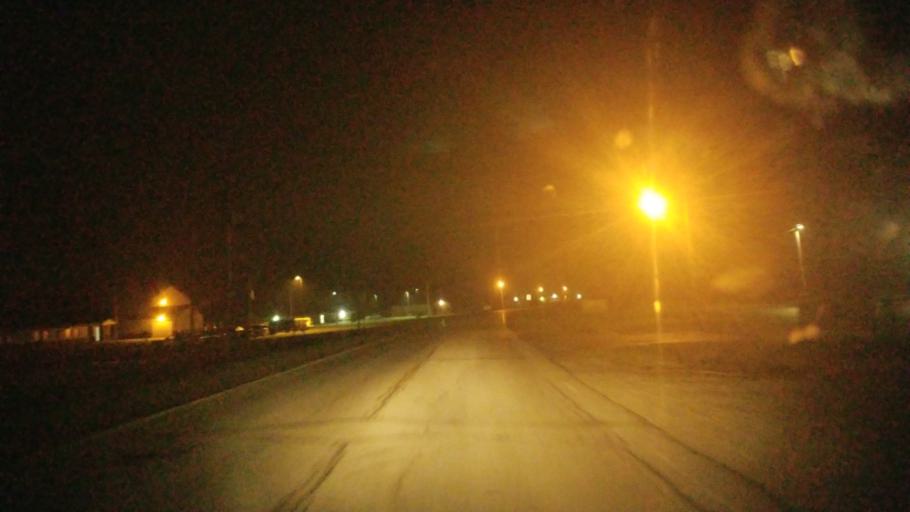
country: US
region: Missouri
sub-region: Pike County
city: Bowling Green
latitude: 39.3470
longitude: -91.2104
